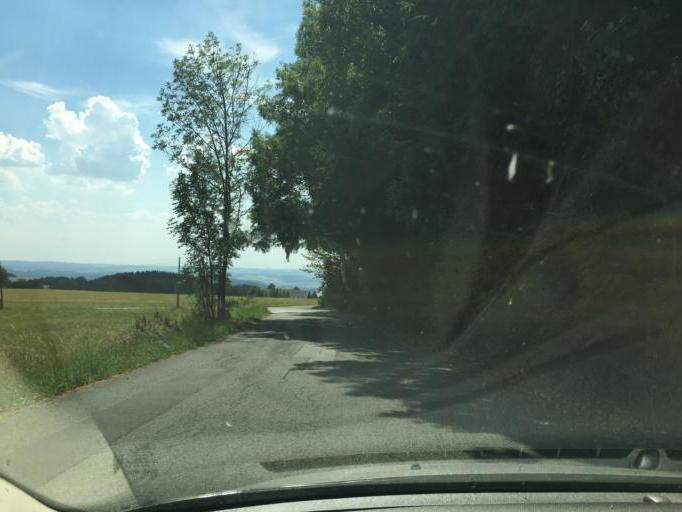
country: CZ
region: Liberecky
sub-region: Okres Semily
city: Ponikla
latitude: 50.6649
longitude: 15.5050
